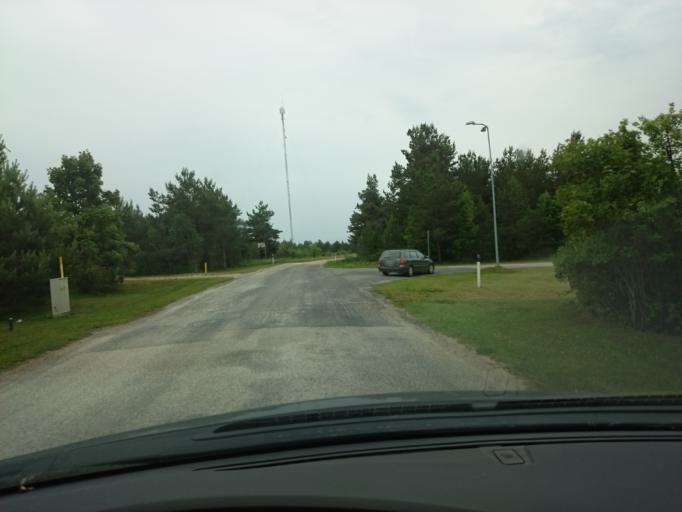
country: EE
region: Saare
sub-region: Orissaare vald
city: Orissaare
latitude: 58.6019
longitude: 23.2362
